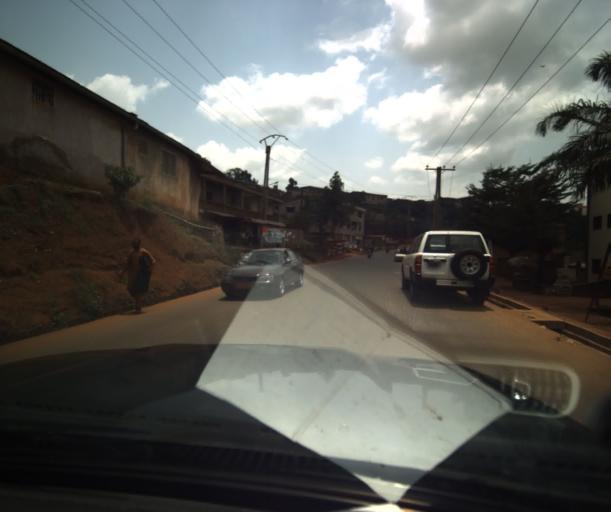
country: CM
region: Centre
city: Yaounde
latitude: 3.8440
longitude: 11.4789
